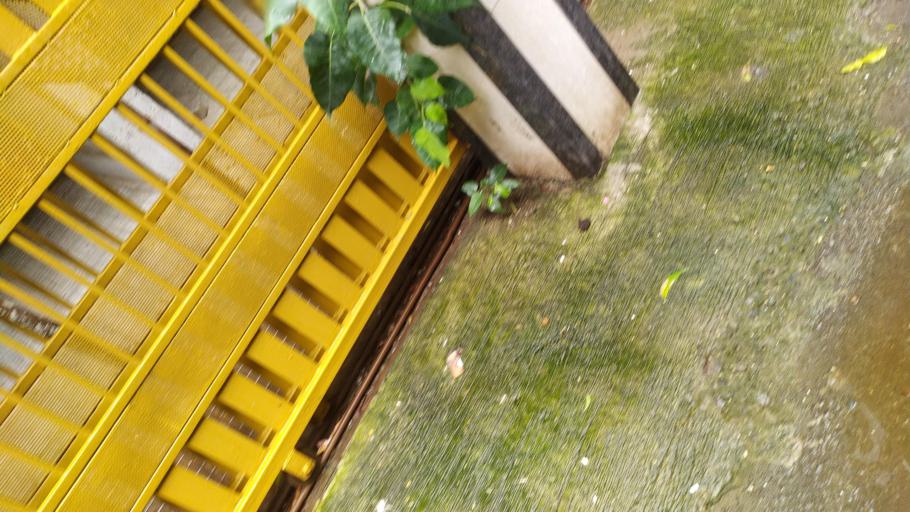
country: IN
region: Maharashtra
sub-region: Mumbai Suburban
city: Borivli
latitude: 19.2421
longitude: 72.8557
